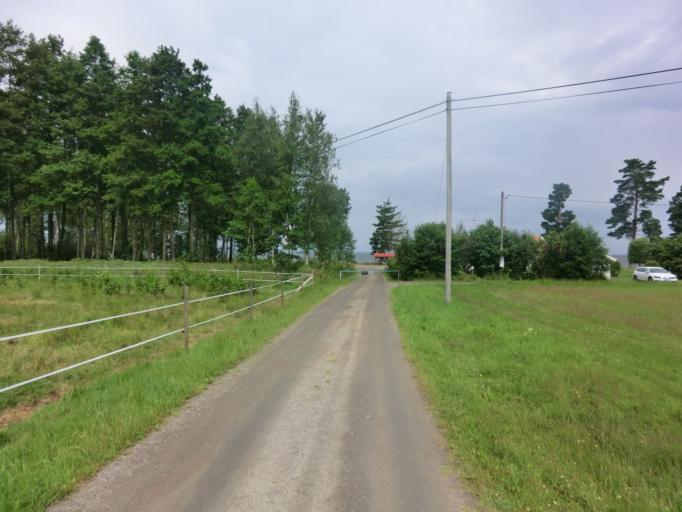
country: SE
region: Vaestra Goetaland
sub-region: Gullspangs Kommun
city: Anderstorp
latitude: 58.9109
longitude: 14.2923
